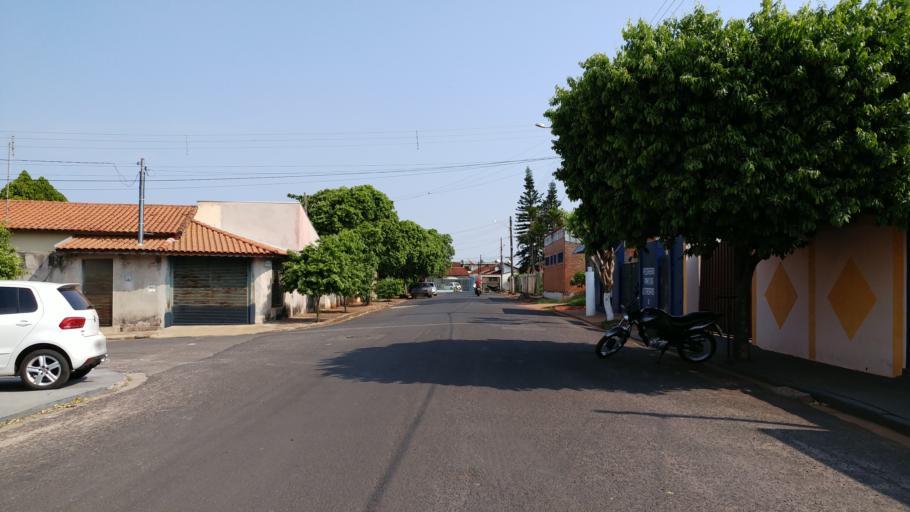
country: BR
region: Sao Paulo
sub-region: Paraguacu Paulista
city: Paraguacu Paulista
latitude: -22.4264
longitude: -50.5795
